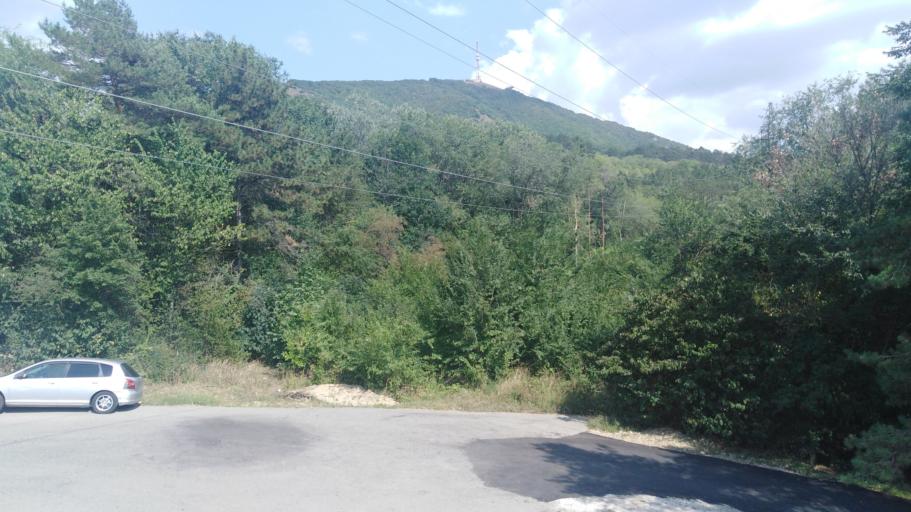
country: RU
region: Stavropol'skiy
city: Pyatigorsk
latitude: 44.0499
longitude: 43.0688
